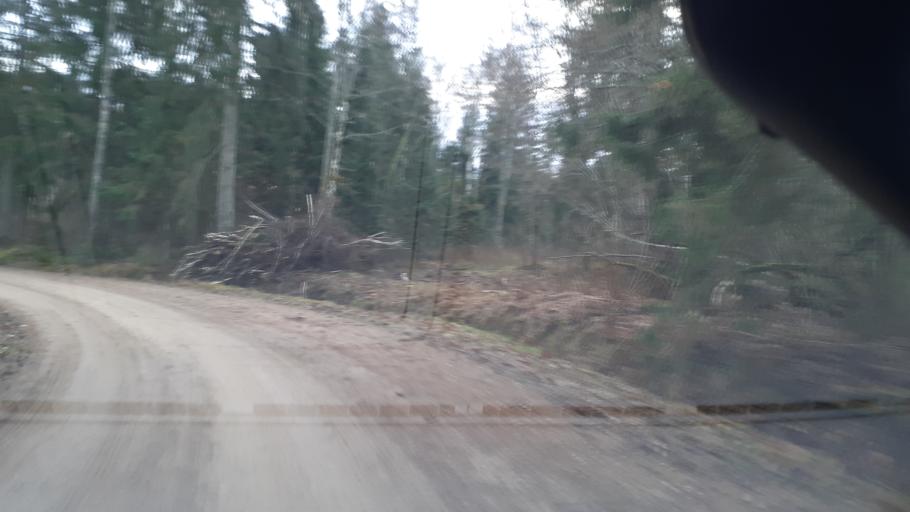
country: LV
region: Kuldigas Rajons
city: Kuldiga
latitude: 56.9010
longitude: 21.9100
